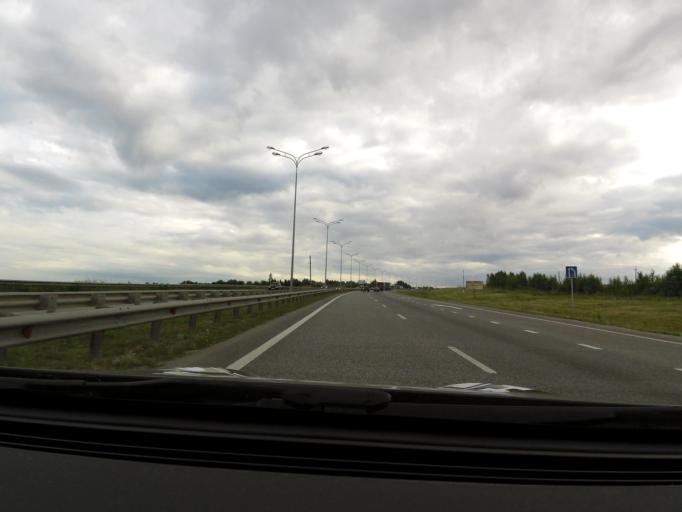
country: RU
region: Tatarstan
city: Osinovo
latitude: 55.7705
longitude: 48.8359
